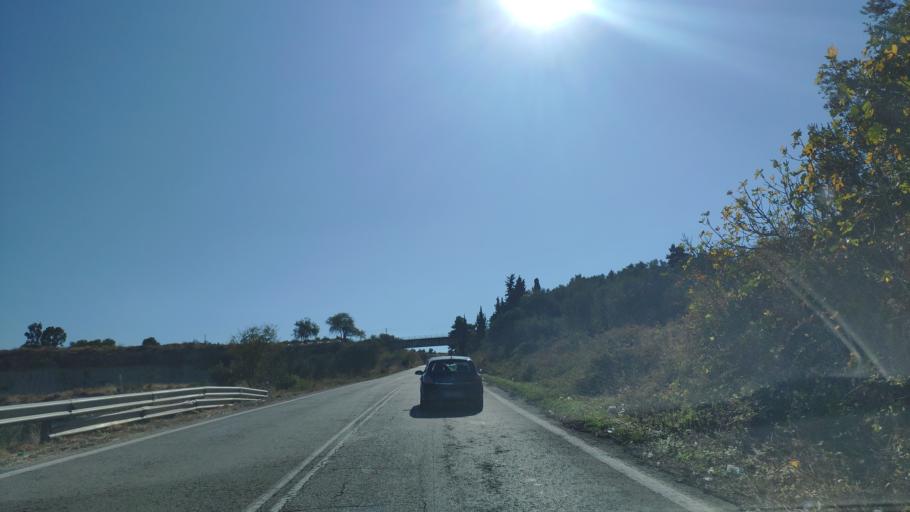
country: GR
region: Peloponnese
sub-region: Nomos Korinthias
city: Arkhaia Korinthos
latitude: 37.9150
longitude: 22.8953
